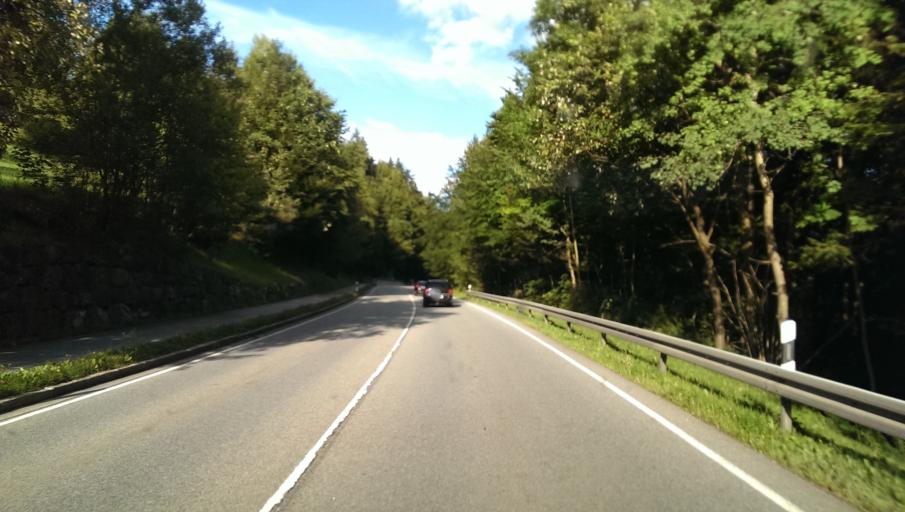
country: DE
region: Bavaria
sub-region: Upper Bavaria
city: Garmisch-Partenkirchen
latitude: 47.4869
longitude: 11.1533
